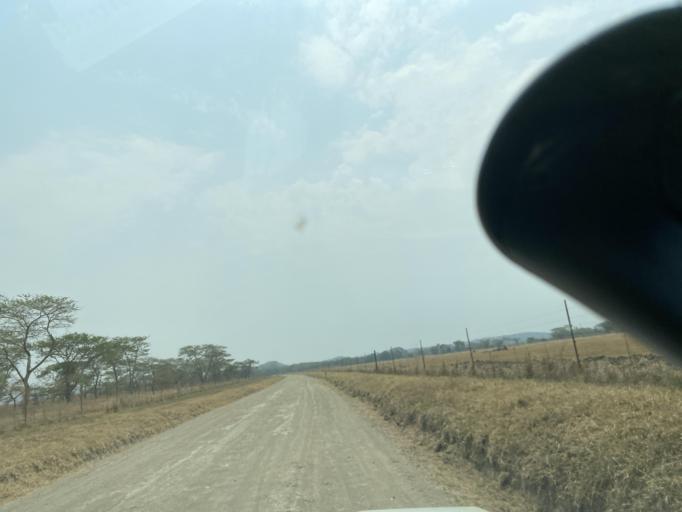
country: ZM
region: Lusaka
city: Kafue
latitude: -15.5803
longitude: 28.1202
